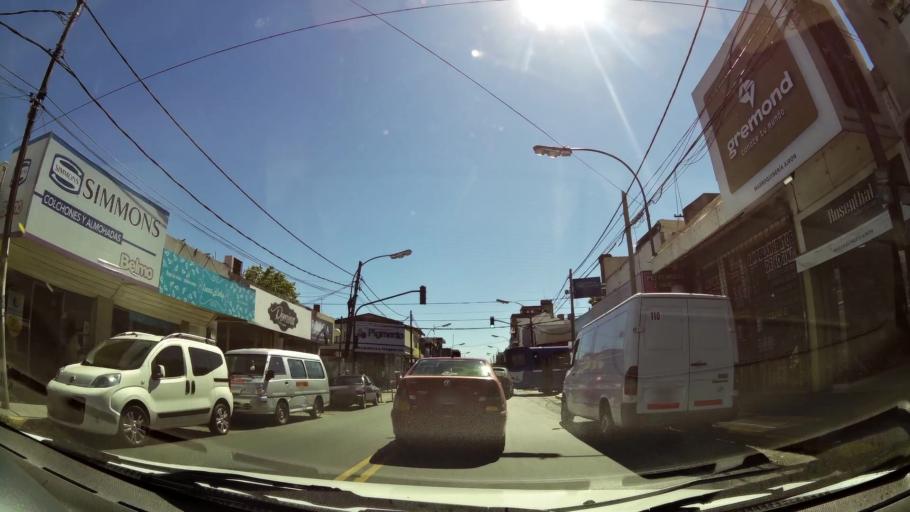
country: AR
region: Buenos Aires
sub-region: Partido de Vicente Lopez
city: Olivos
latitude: -34.5286
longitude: -58.5205
